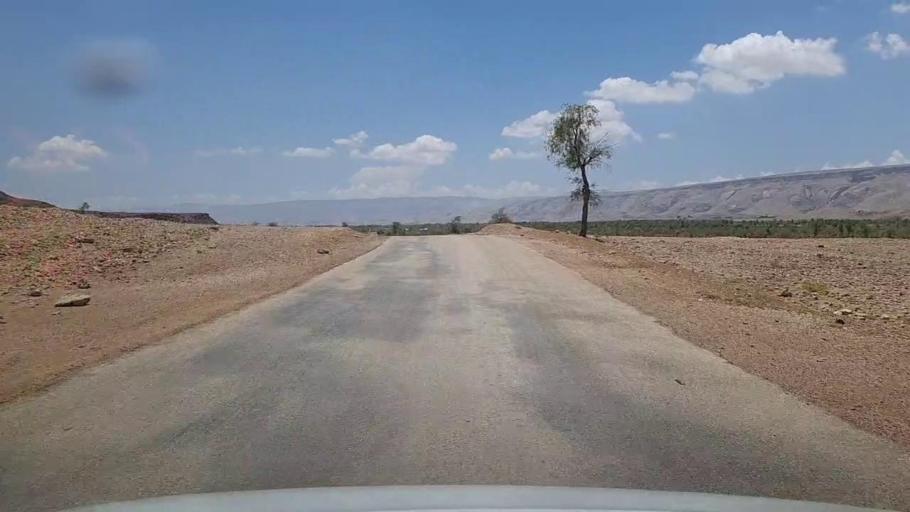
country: PK
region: Sindh
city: Bhan
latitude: 26.3018
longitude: 67.5361
